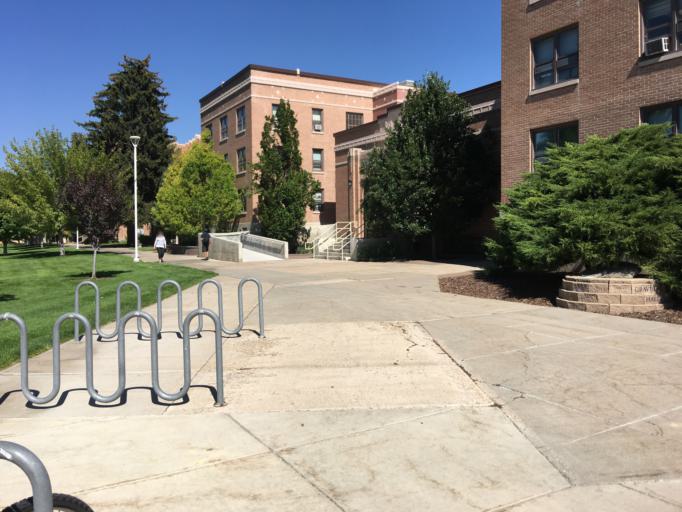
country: US
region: Idaho
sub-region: Bannock County
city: Pocatello
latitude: 42.8610
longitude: -112.4332
